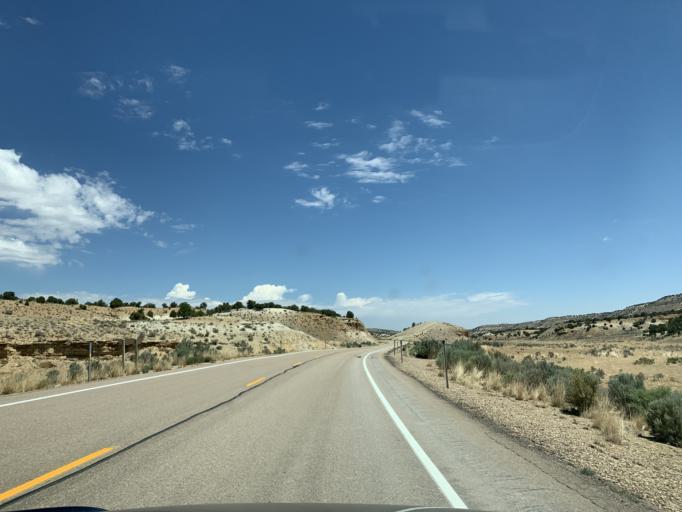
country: US
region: Utah
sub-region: Duchesne County
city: Duchesne
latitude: 39.9341
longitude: -110.2193
